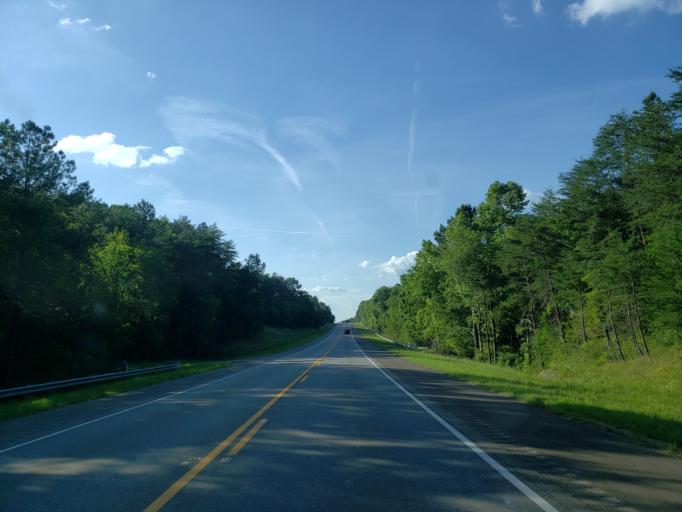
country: US
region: Georgia
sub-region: Murray County
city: Chatsworth
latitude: 34.6778
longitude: -84.7266
